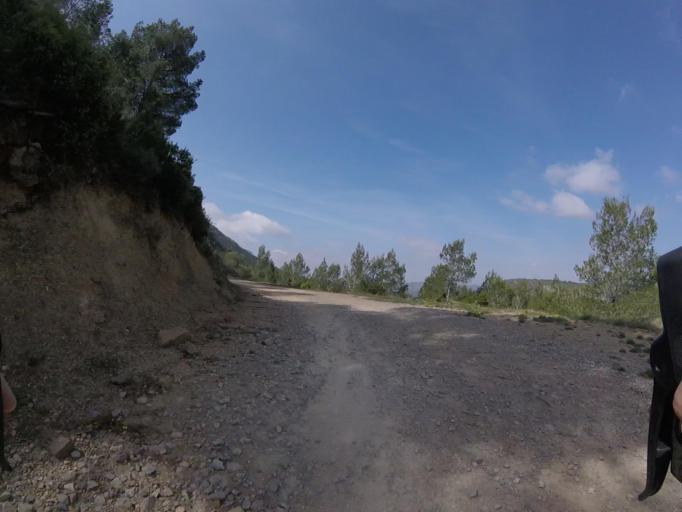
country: ES
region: Valencia
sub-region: Provincia de Castello
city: Benicassim
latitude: 40.0997
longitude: 0.0423
